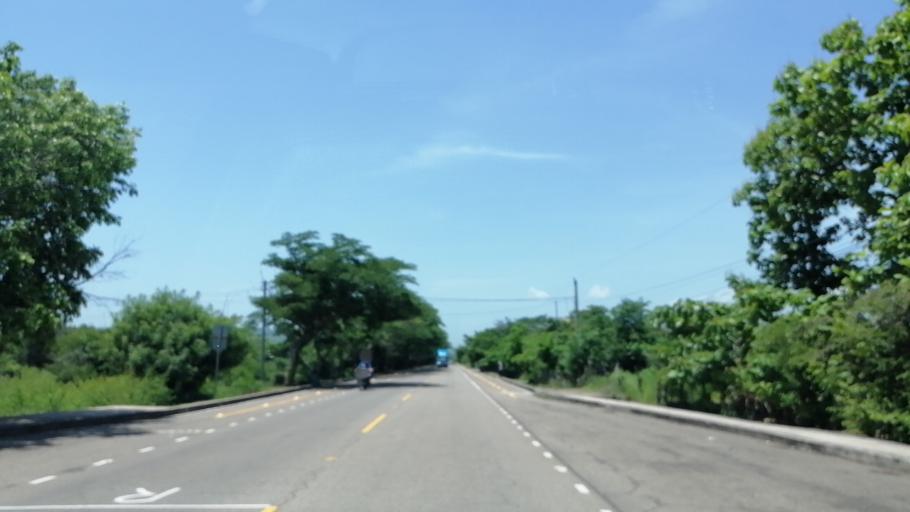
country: SV
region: Chalatenango
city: Nueva Concepcion
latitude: 14.1460
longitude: -89.3035
